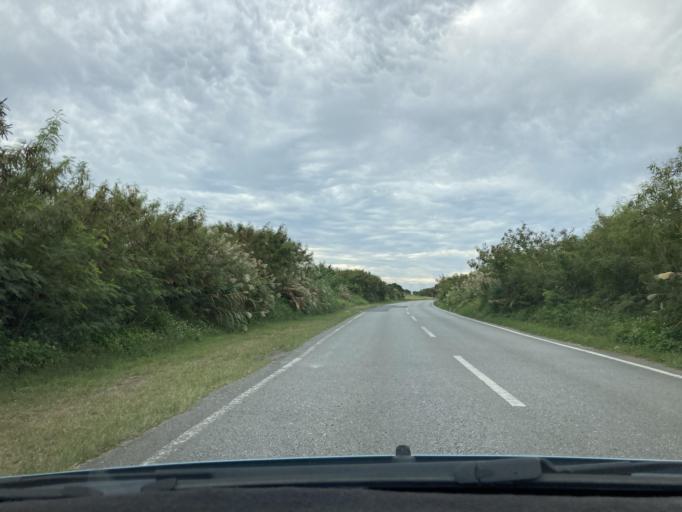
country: JP
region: Okinawa
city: Okinawa
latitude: 26.3895
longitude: 127.7410
